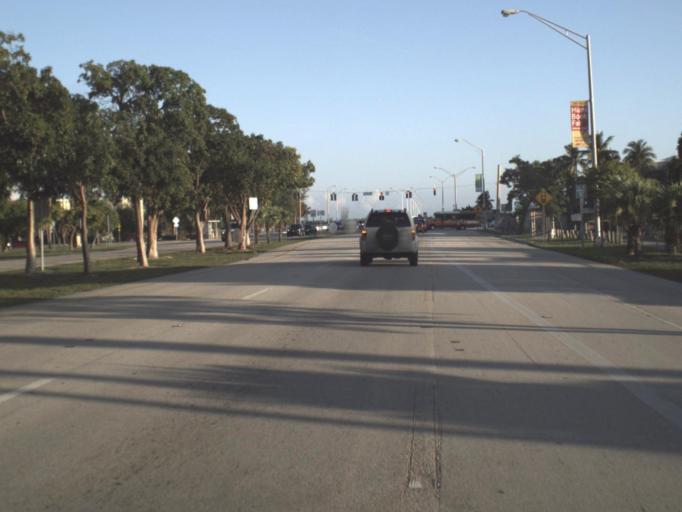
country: US
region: Florida
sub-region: Miami-Dade County
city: Key Biscayne
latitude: 25.7346
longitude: -80.1635
